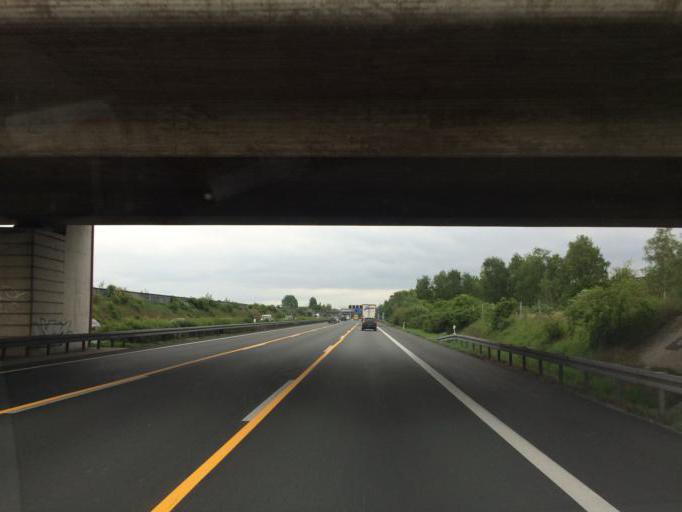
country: DE
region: Lower Saxony
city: Vordorf
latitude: 52.3185
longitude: 10.4997
